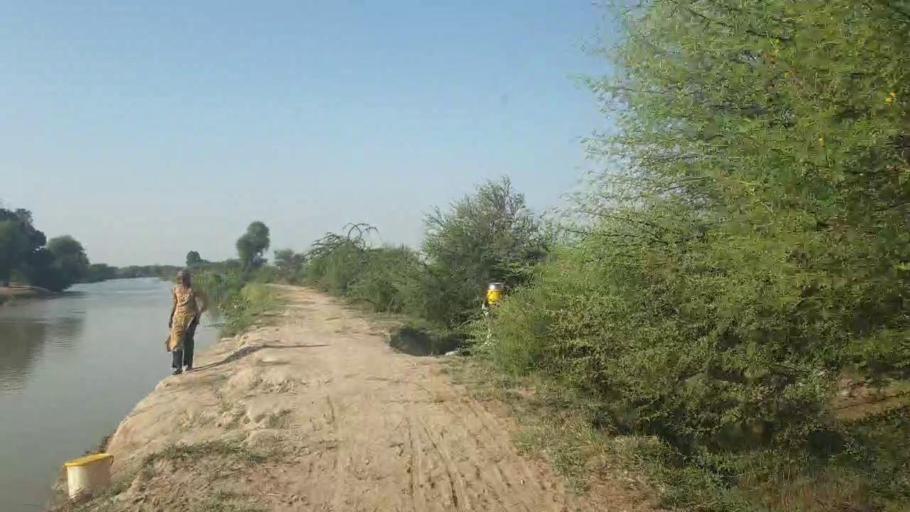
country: PK
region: Sindh
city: Badin
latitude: 24.7118
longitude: 68.8938
